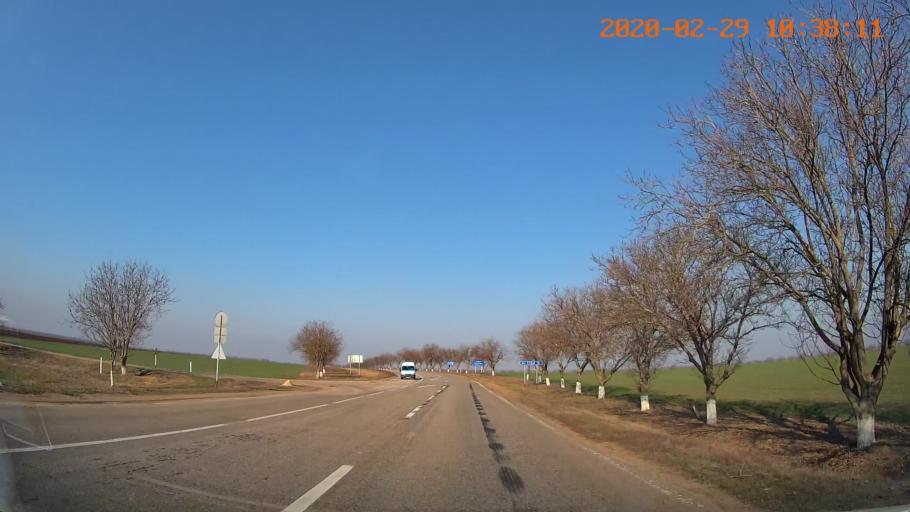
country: MD
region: Anenii Noi
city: Varnita
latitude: 47.0141
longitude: 29.4776
